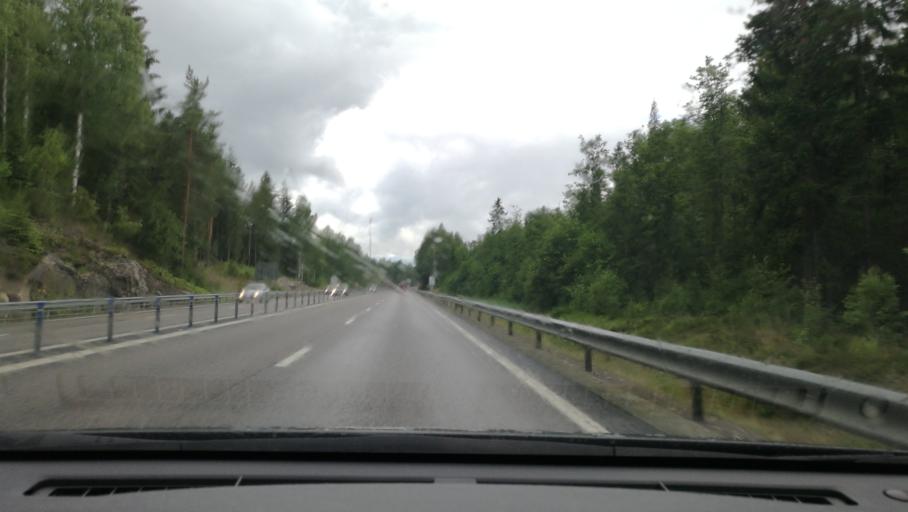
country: SE
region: OEstergoetland
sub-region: Norrkopings Kommun
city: Jursla
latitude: 58.8034
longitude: 16.1526
